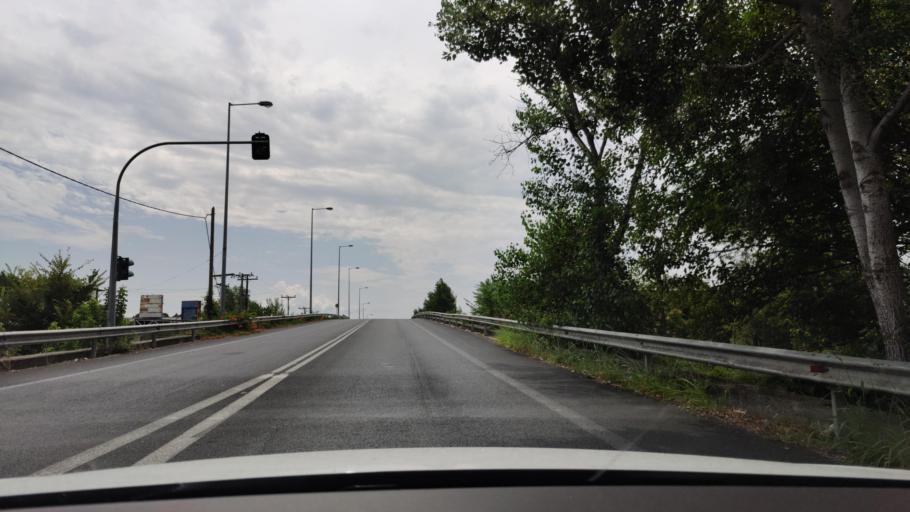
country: GR
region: Central Macedonia
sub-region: Nomos Serron
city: Serres
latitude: 41.0749
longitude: 23.5403
